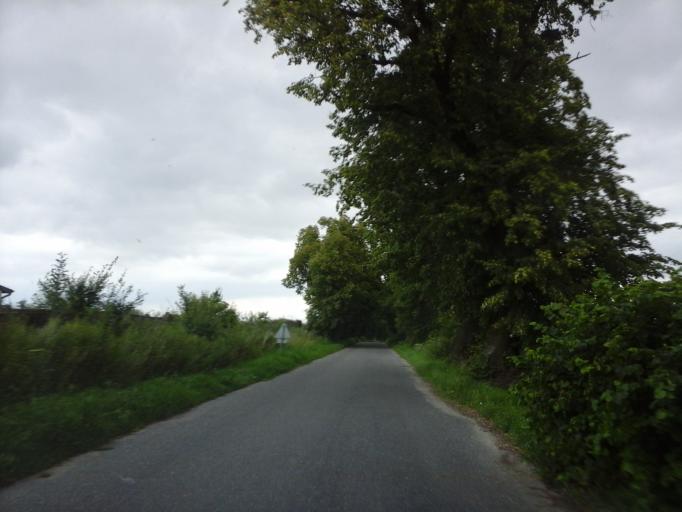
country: PL
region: West Pomeranian Voivodeship
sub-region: Powiat choszczenski
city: Krzecin
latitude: 53.0582
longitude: 15.4810
